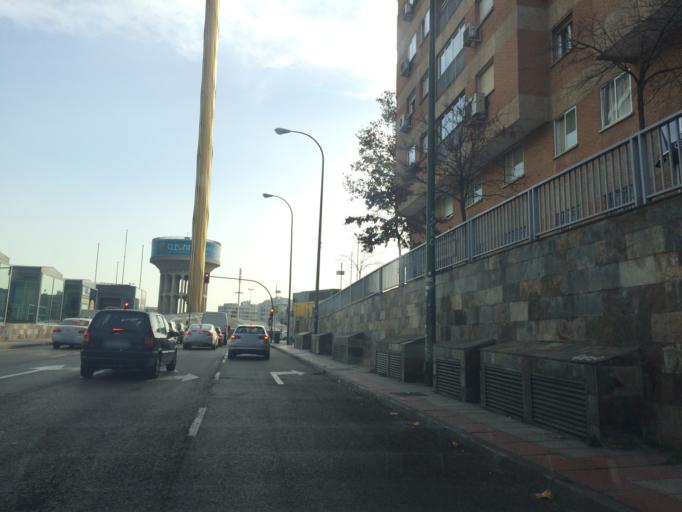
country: ES
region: Madrid
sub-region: Provincia de Madrid
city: Chamartin
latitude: 40.4667
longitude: -3.6908
